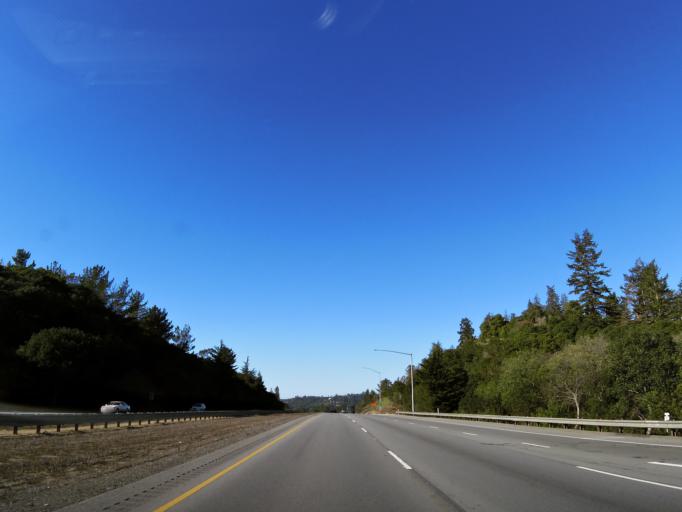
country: US
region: California
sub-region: Santa Cruz County
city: La Selva Beach
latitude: 36.9638
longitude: -121.8658
